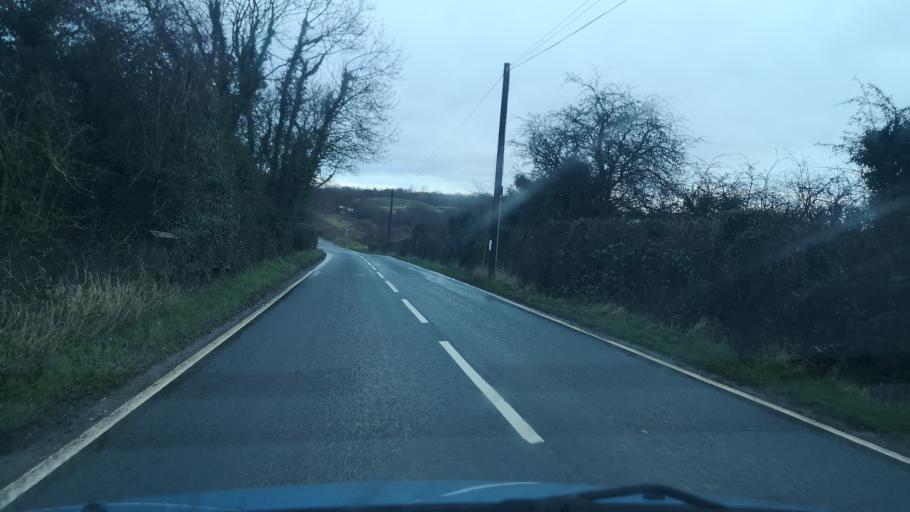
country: GB
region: England
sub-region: City and Borough of Wakefield
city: Fitzwilliam
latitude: 53.6428
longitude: -1.3961
